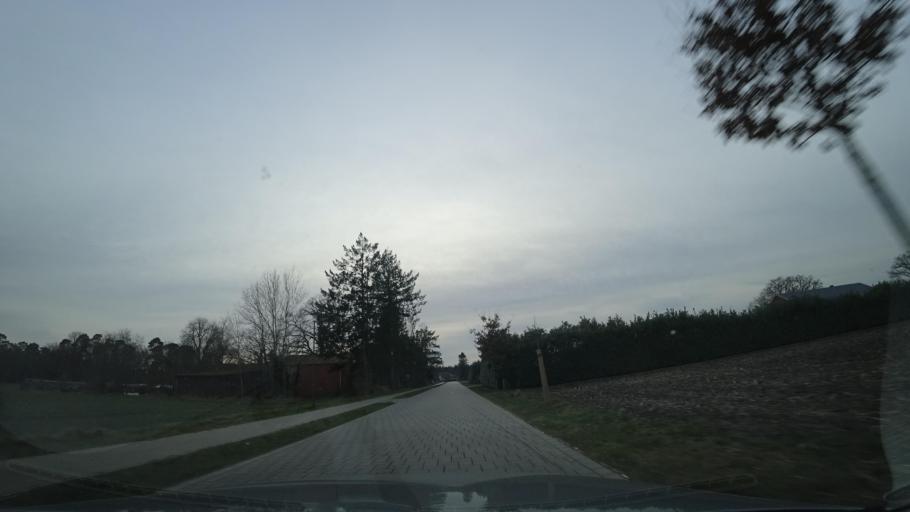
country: DE
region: Lower Saxony
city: Wardenburg
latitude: 53.0444
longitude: 8.2864
